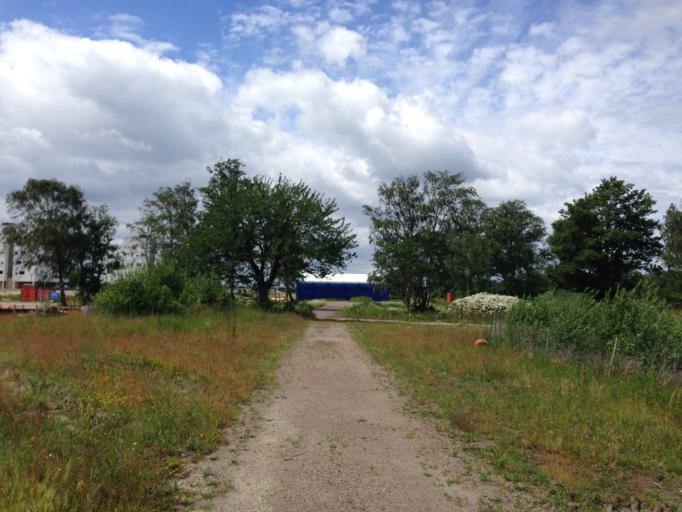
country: SE
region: Skane
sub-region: Lomma Kommun
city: Lomma
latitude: 55.6825
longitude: 13.0634
